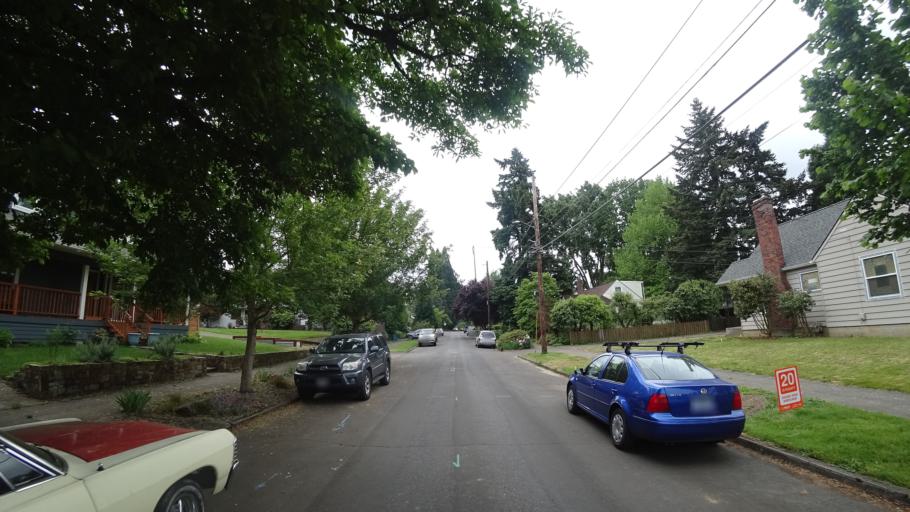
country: US
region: Oregon
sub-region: Clackamas County
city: Milwaukie
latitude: 45.4857
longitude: -122.6247
